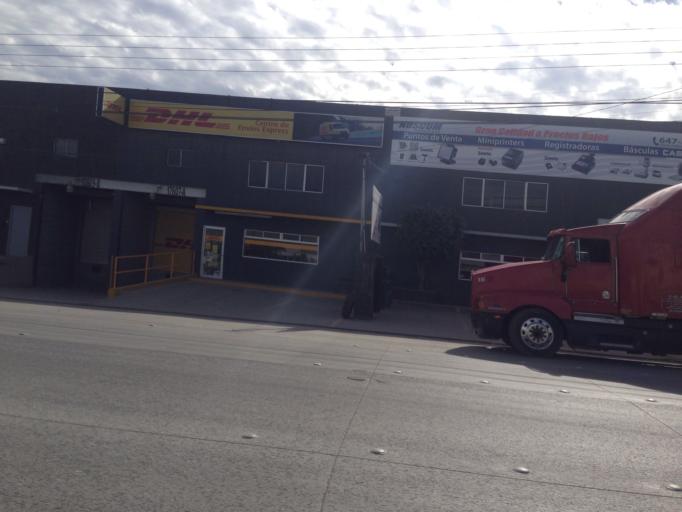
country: MX
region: Baja California
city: Tijuana
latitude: 32.5431
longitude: -116.9424
